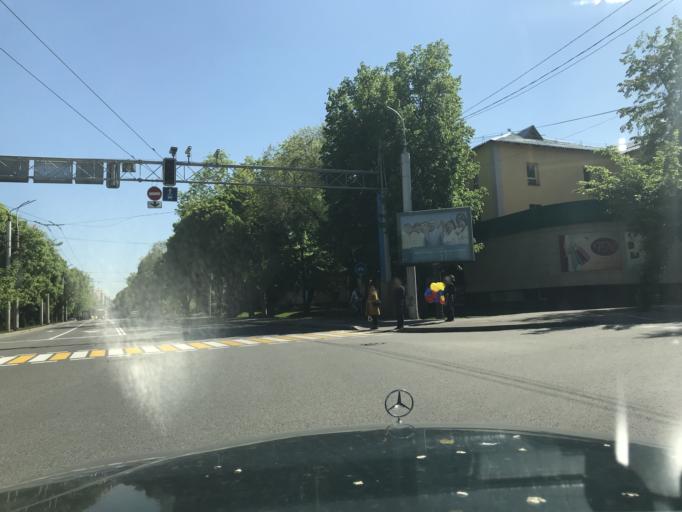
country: KZ
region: Almaty Qalasy
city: Almaty
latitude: 43.2268
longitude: 76.9281
